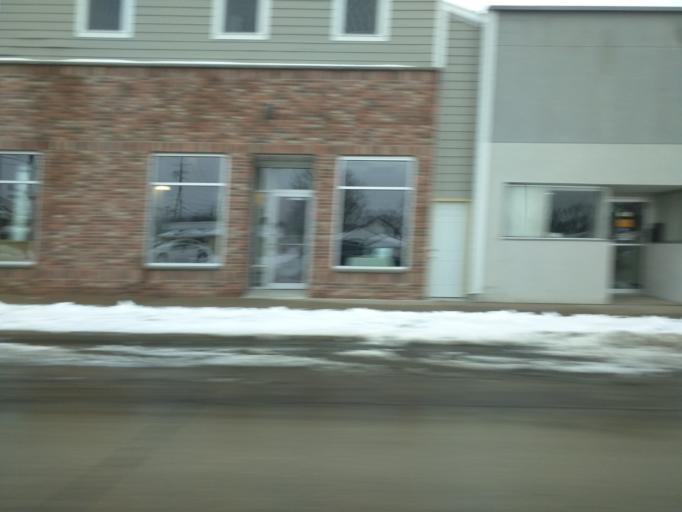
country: US
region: Wisconsin
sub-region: La Crosse County
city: North La Crosse
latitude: 43.8349
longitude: -91.2482
